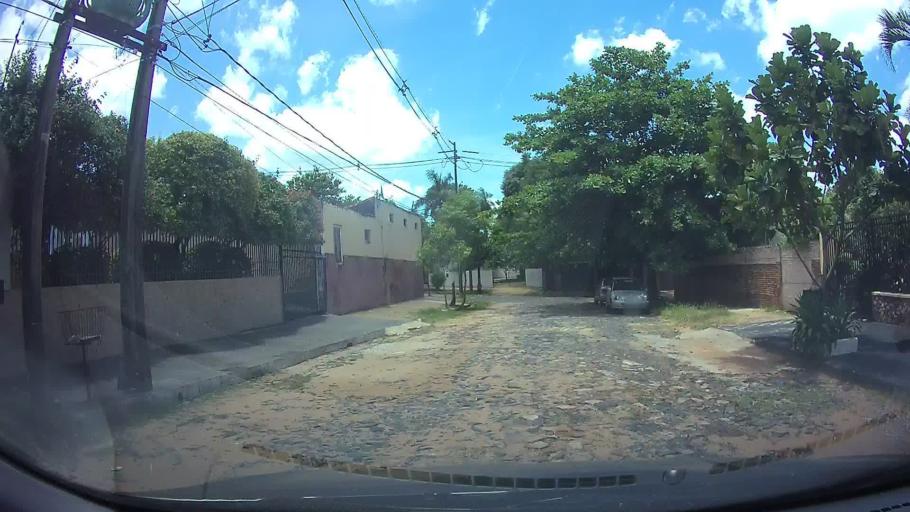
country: PY
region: Asuncion
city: Asuncion
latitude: -25.2728
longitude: -57.5903
